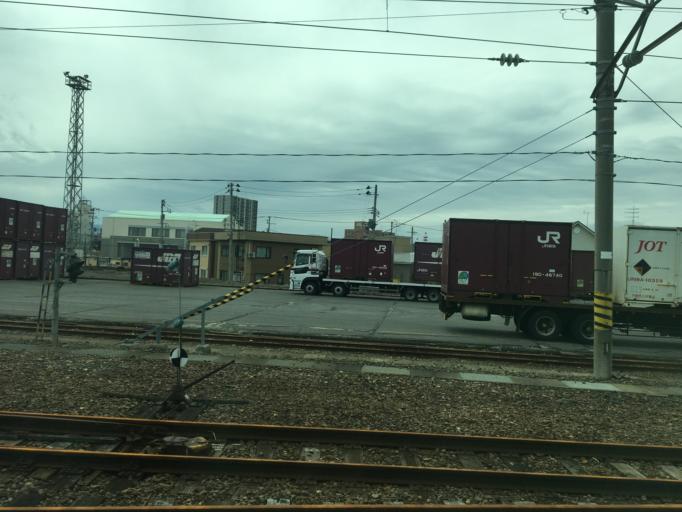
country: JP
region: Aomori
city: Hirosaki
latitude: 40.6029
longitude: 140.4838
